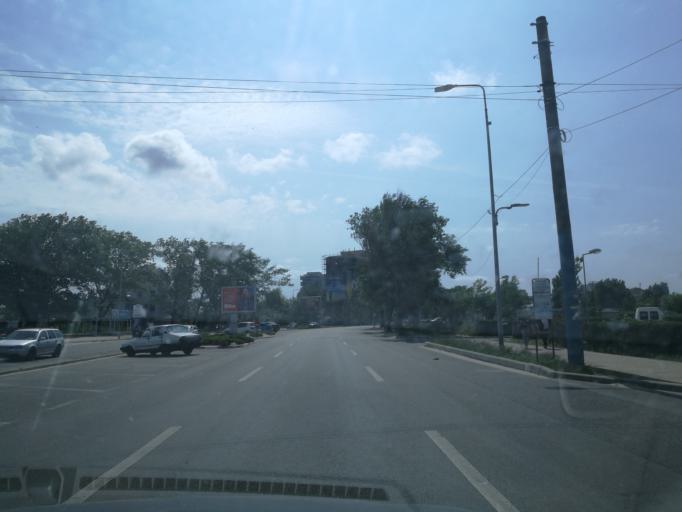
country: RO
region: Constanta
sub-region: Municipiul Constanta
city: Constanta
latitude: 44.2170
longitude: 28.6394
